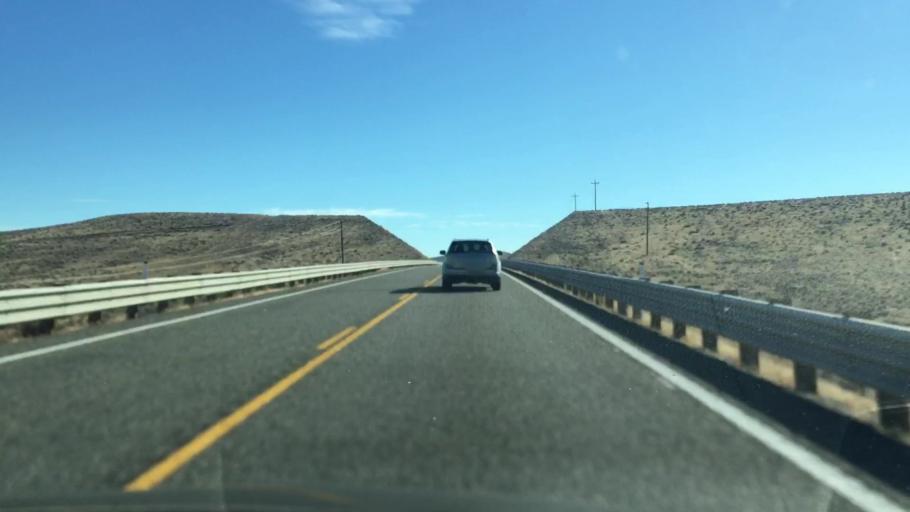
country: US
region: Nevada
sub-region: Lyon County
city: Silver Springs
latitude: 39.2167
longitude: -119.2213
